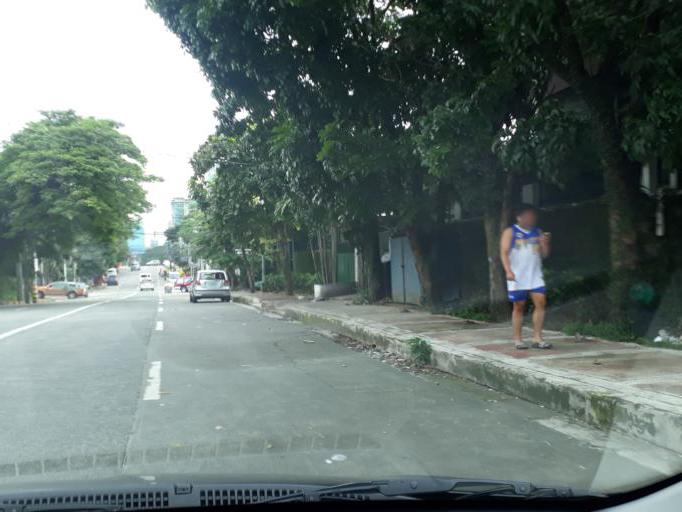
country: PH
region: Calabarzon
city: Del Monte
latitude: 14.6311
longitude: 121.0323
